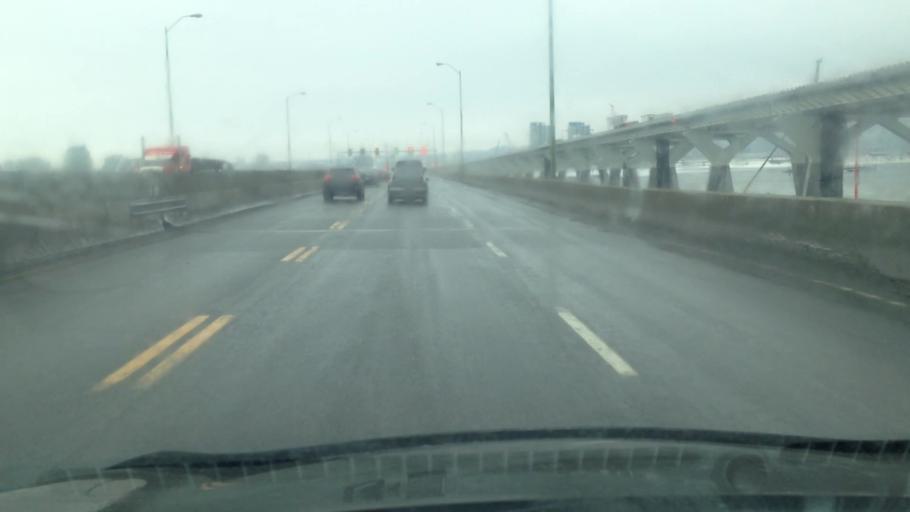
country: CA
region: Quebec
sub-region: Monteregie
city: Brossard
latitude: 45.4680
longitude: -73.5117
